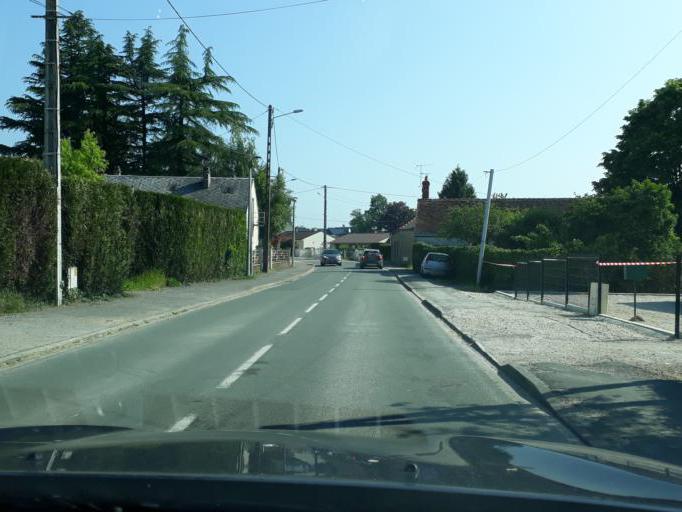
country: FR
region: Centre
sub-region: Departement du Loiret
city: Trainou
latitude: 47.9709
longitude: 2.1023
